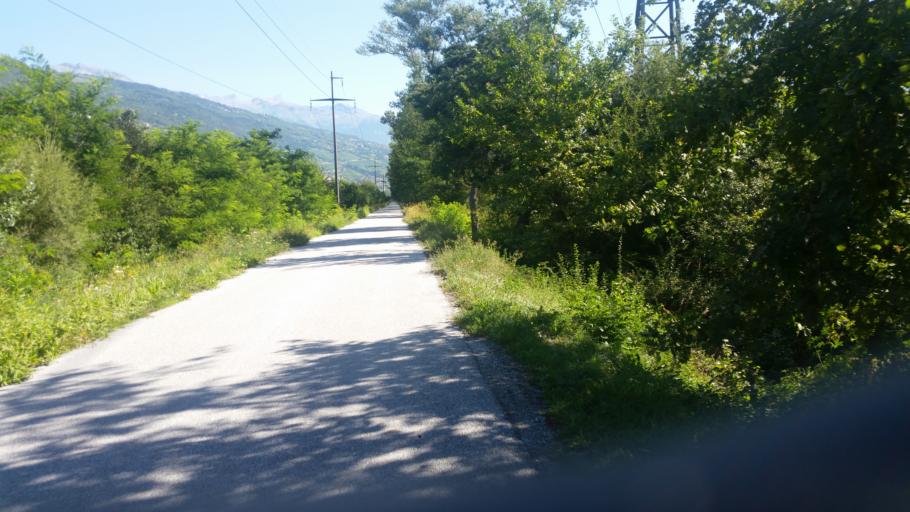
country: CH
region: Valais
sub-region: Sion District
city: Saint-Leonard
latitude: 46.2474
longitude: 7.4320
